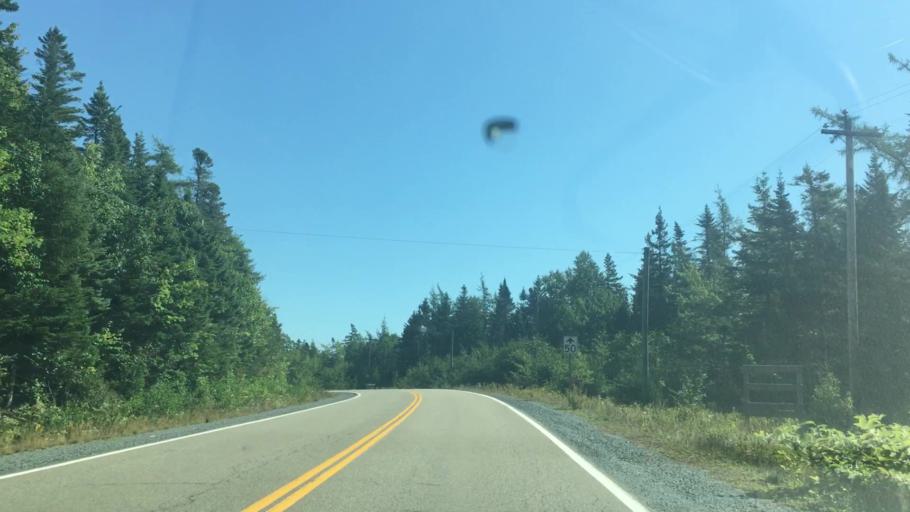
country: CA
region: Nova Scotia
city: Antigonish
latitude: 45.1445
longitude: -61.9944
